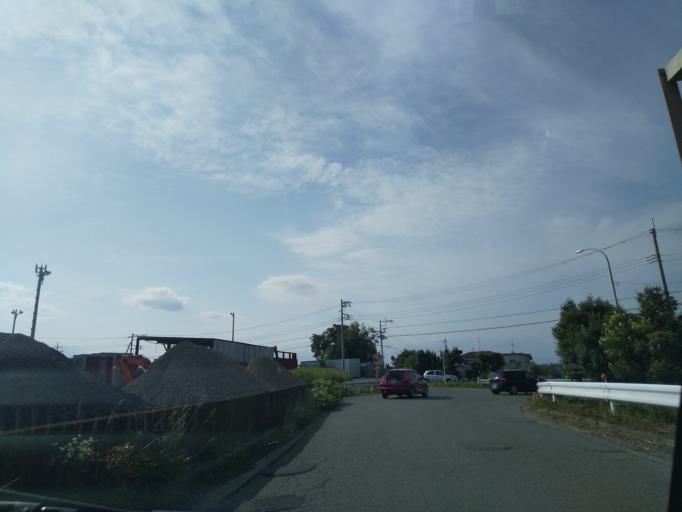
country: JP
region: Kanagawa
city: Zama
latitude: 35.4796
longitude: 139.3800
